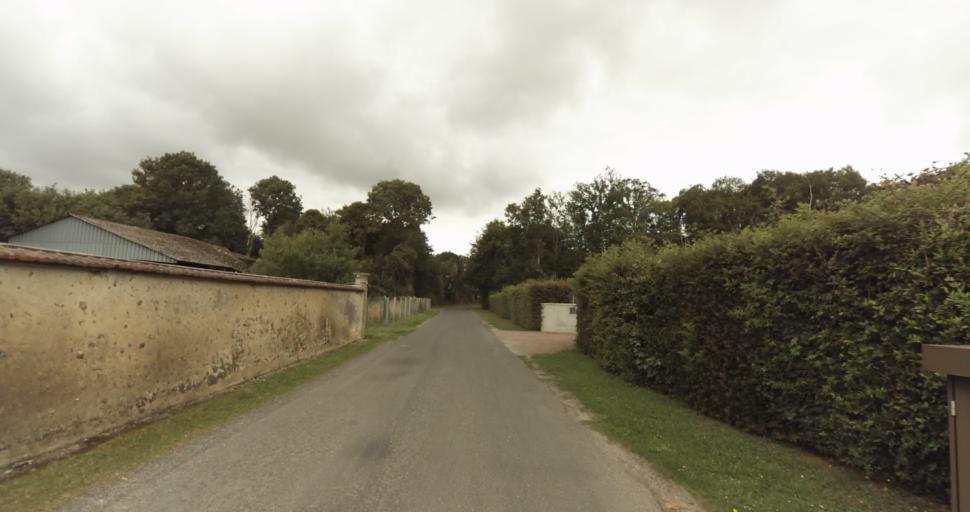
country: FR
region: Haute-Normandie
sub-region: Departement de l'Eure
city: Menilles
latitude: 49.0060
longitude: 1.2732
